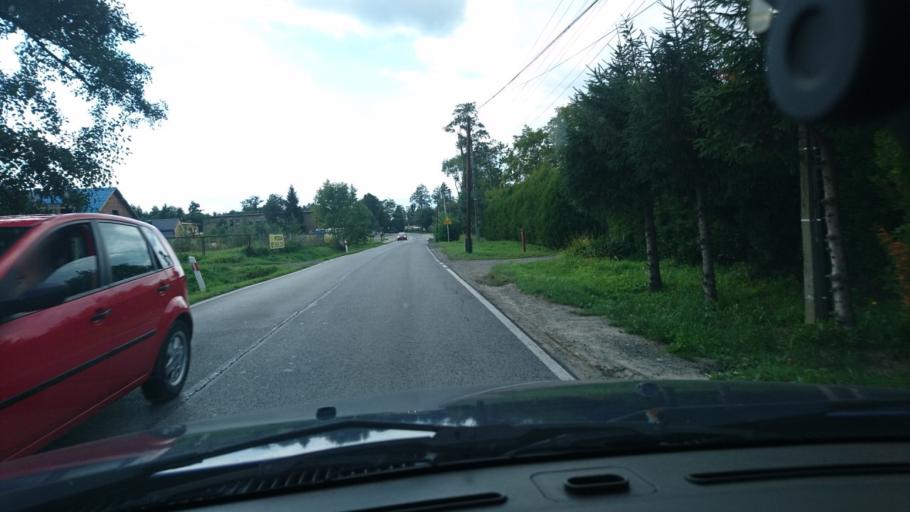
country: PL
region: Silesian Voivodeship
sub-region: Powiat bielski
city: Ligota
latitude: 49.9010
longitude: 18.9733
